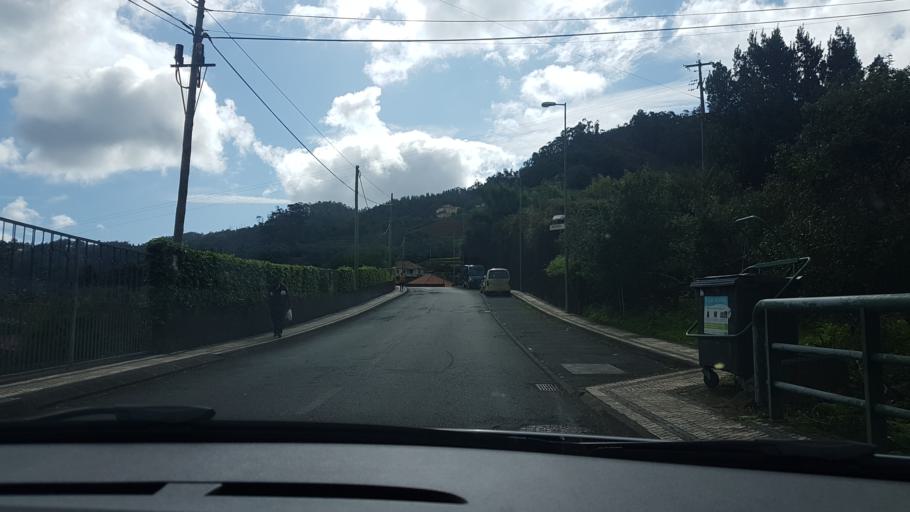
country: PT
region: Madeira
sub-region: Santa Cruz
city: Santa Cruz
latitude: 32.7362
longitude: -16.8189
